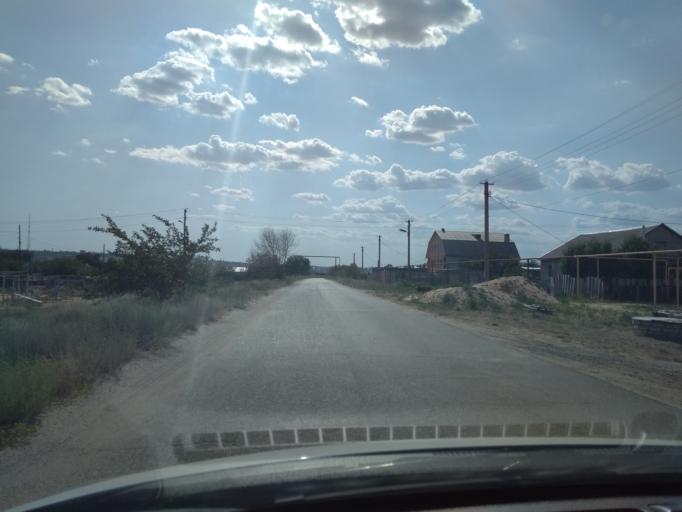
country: RU
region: Volgograd
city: Vodstroy
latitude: 48.8038
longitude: 44.5335
